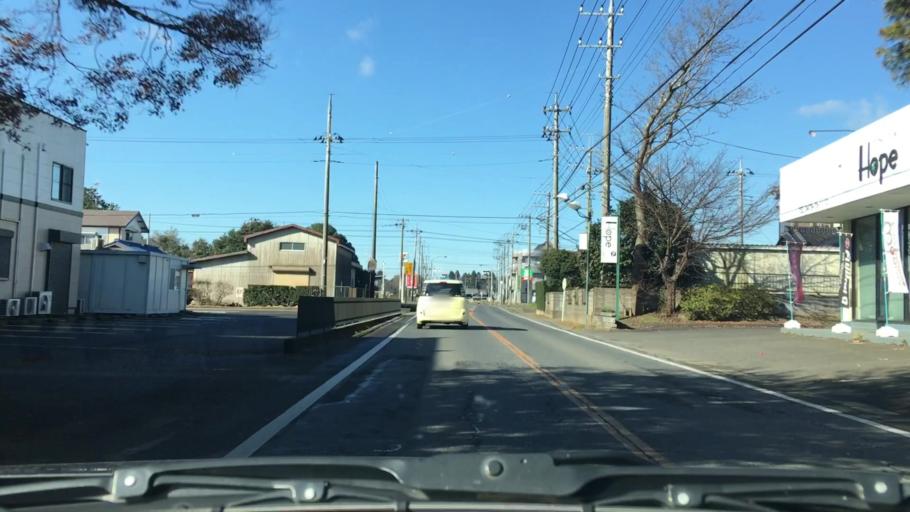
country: JP
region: Chiba
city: Sawara
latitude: 35.7986
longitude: 140.4468
